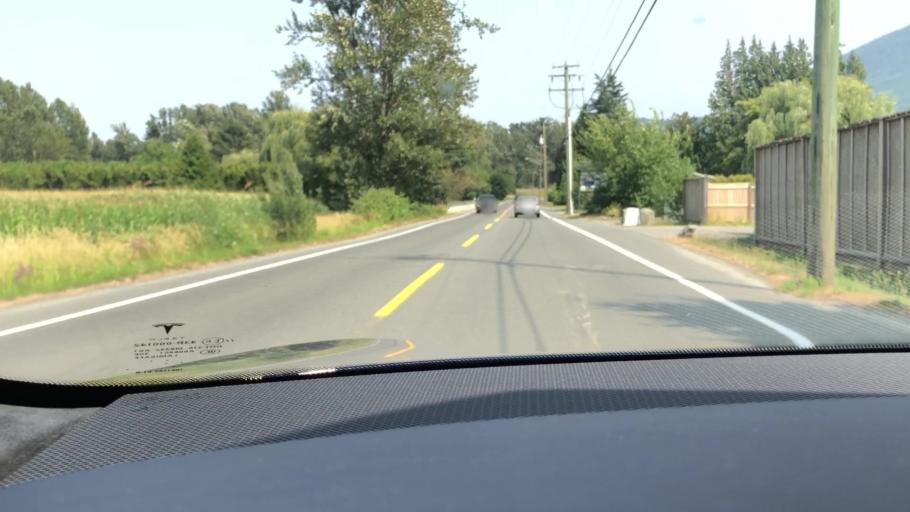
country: CA
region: British Columbia
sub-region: Fraser Valley Regional District
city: Chilliwack
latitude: 49.0892
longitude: -122.0708
